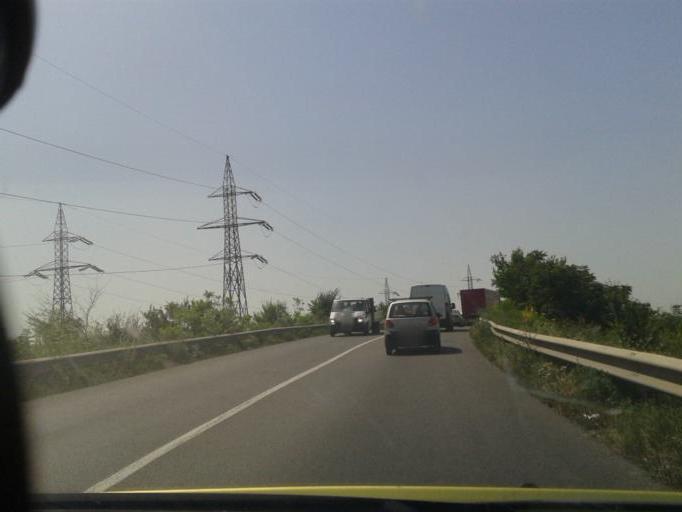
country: RO
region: Ilfov
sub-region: Comuna Glina
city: Catelu
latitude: 44.4239
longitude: 26.2362
